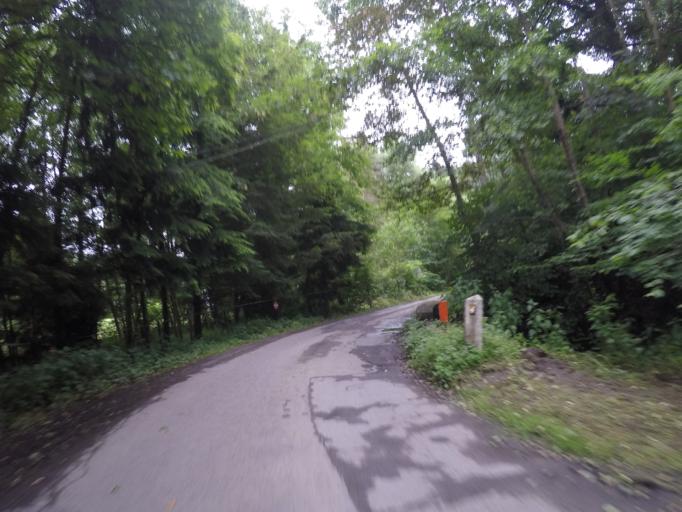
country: BE
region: Wallonia
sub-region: Province de Namur
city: Yvoir
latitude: 50.3330
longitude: 4.9286
